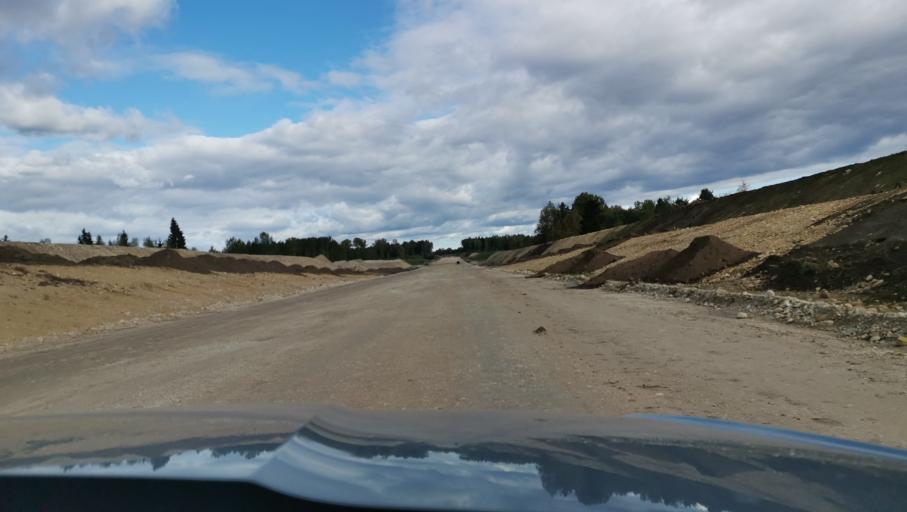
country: EE
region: Harju
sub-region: Keila linn
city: Keila
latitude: 59.1409
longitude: 24.4905
